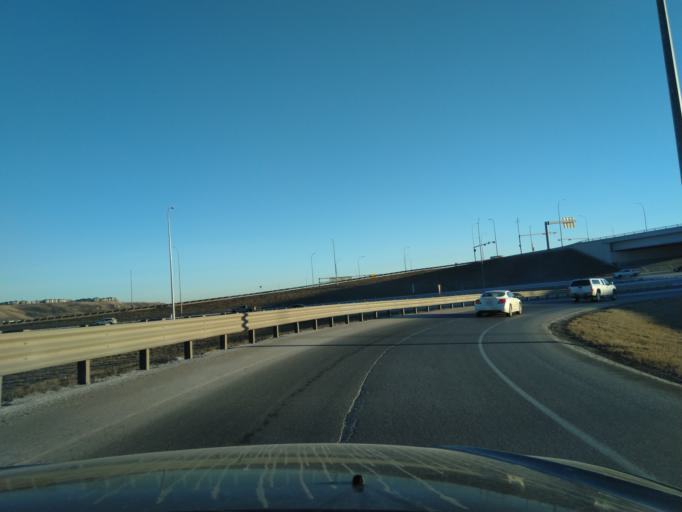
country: CA
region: Alberta
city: Calgary
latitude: 51.1582
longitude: -114.1159
